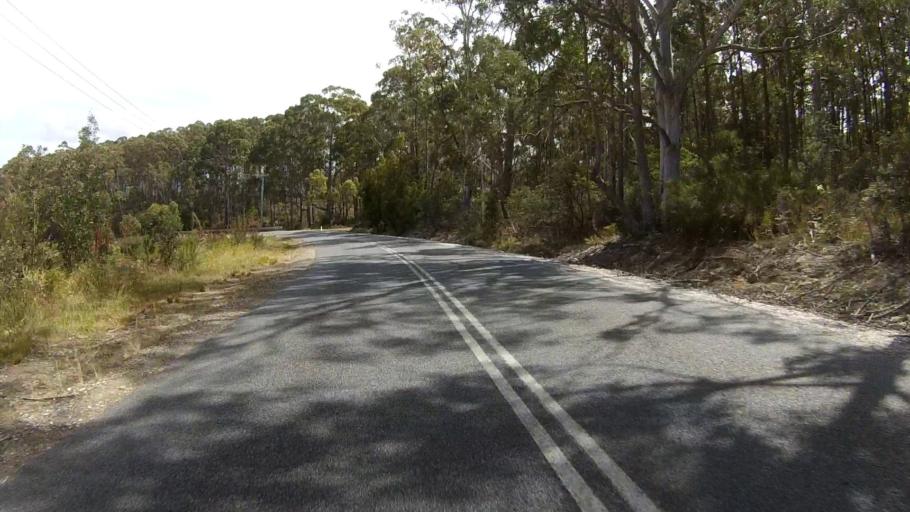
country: AU
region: Tasmania
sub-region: Huon Valley
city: Cygnet
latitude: -43.2216
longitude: 147.1278
